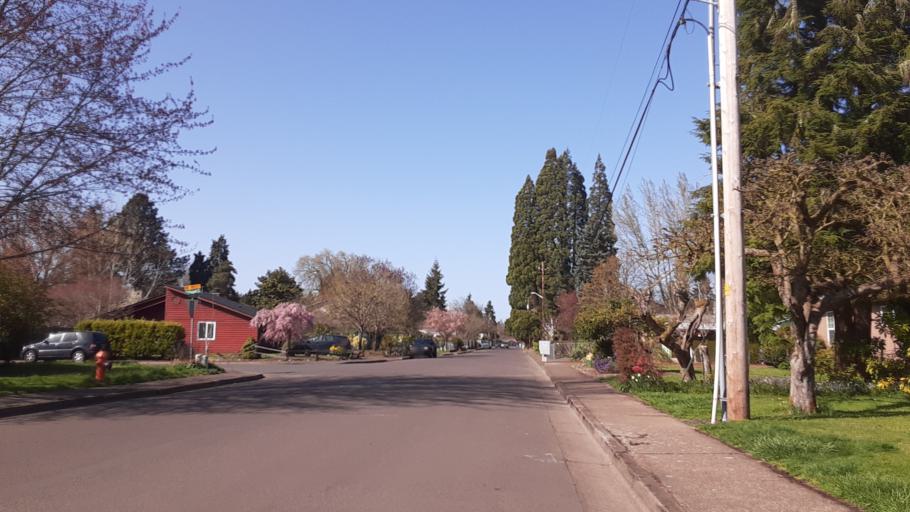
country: US
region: Oregon
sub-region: Benton County
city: Corvallis
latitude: 44.5405
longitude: -123.2604
